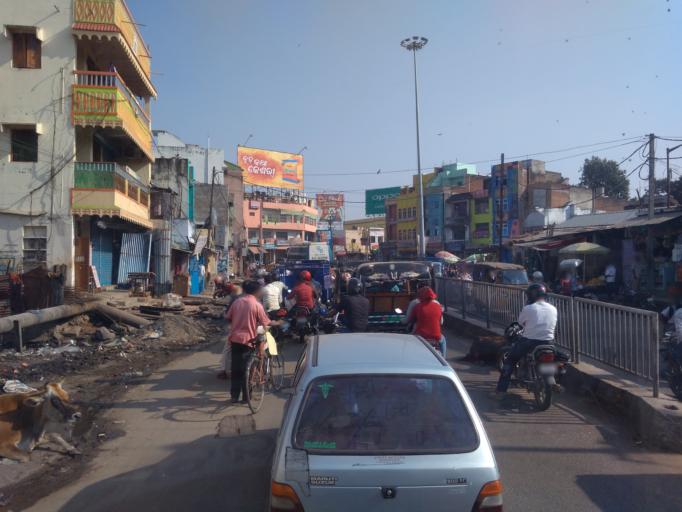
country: IN
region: Odisha
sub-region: Ganjam
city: Brahmapur
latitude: 19.3154
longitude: 84.7937
